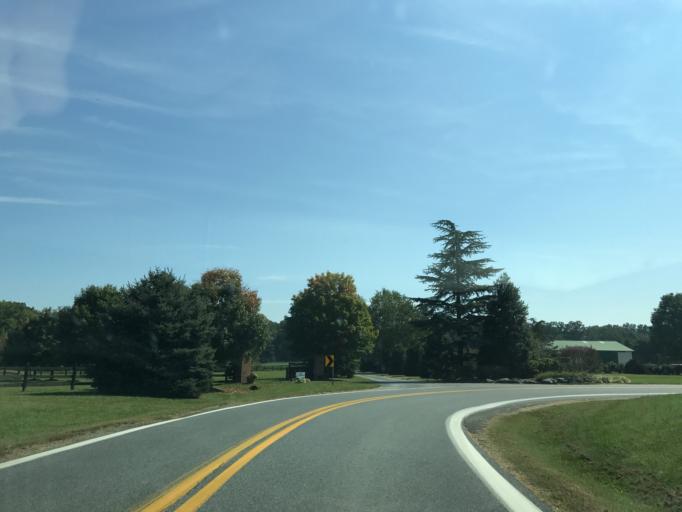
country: US
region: Delaware
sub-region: New Castle County
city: Middletown
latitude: 39.5069
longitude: -75.7993
